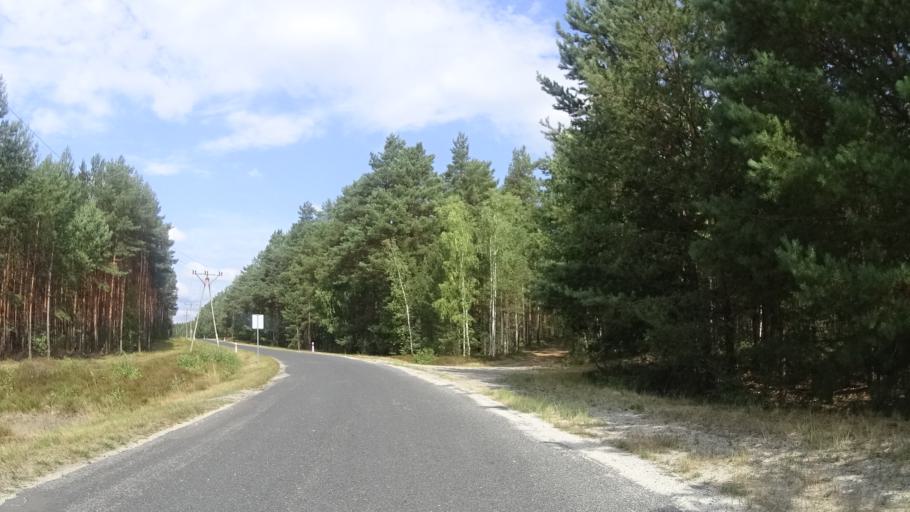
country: PL
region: Lubusz
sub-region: Powiat zarski
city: Leknica
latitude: 51.5285
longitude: 14.8190
